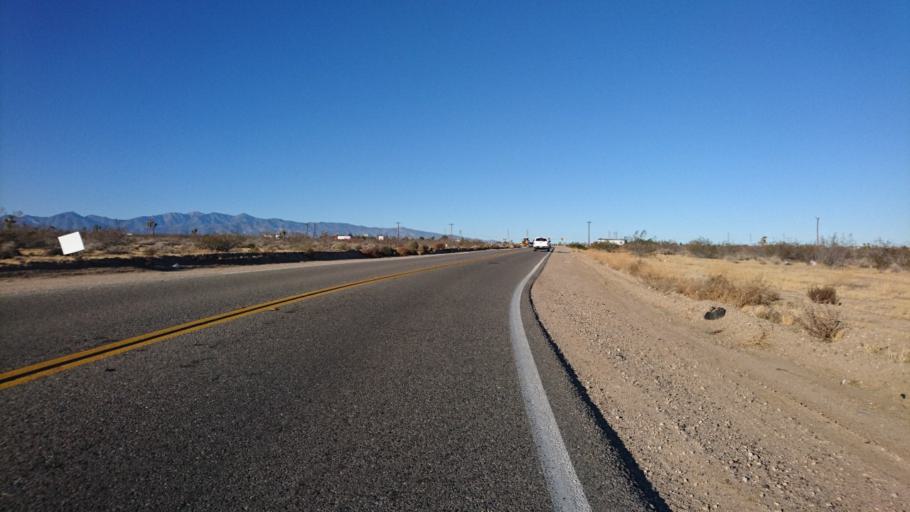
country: US
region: California
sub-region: San Bernardino County
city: Mountain View Acres
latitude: 34.4544
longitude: -117.3555
